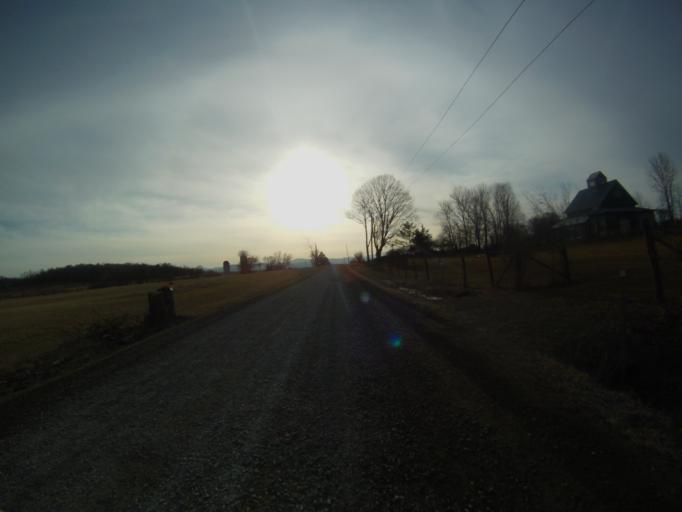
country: US
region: Vermont
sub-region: Addison County
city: Middlebury (village)
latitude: 44.0402
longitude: -73.2840
